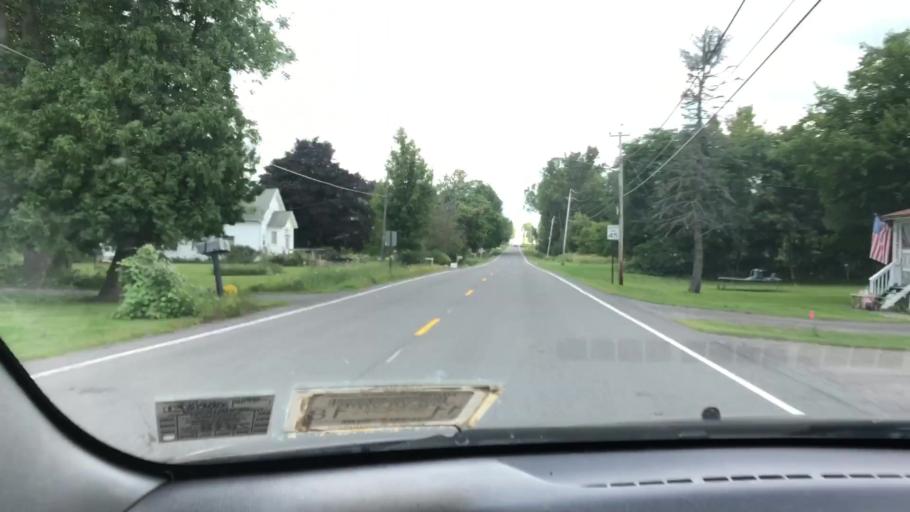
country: US
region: New York
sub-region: Wayne County
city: Macedon
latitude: 43.0968
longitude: -77.3206
